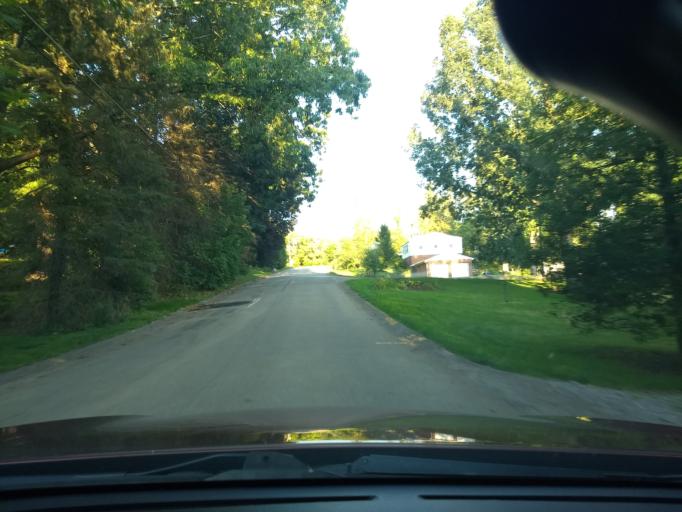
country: US
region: Pennsylvania
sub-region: Allegheny County
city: Gibsonia
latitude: 40.6461
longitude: -79.9581
